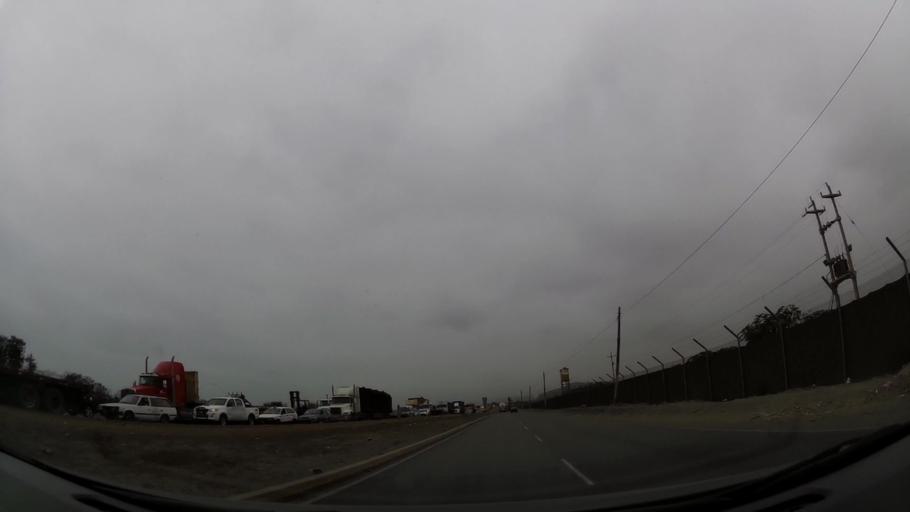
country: PE
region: Callao
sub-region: Callao
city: Callao
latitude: -12.0165
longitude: -77.1295
